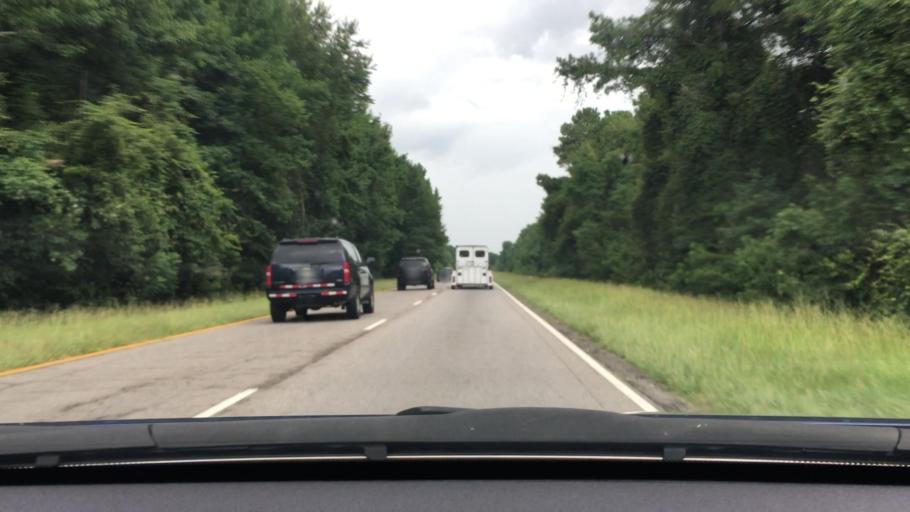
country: US
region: South Carolina
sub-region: Sumter County
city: Stateburg
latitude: 33.9482
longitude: -80.6146
